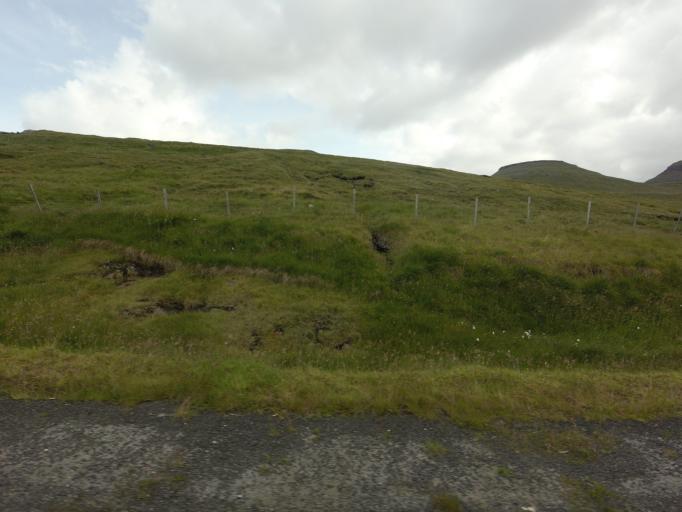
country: FO
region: Eysturoy
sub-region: Eidi
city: Eidi
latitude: 62.2202
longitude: -7.0008
